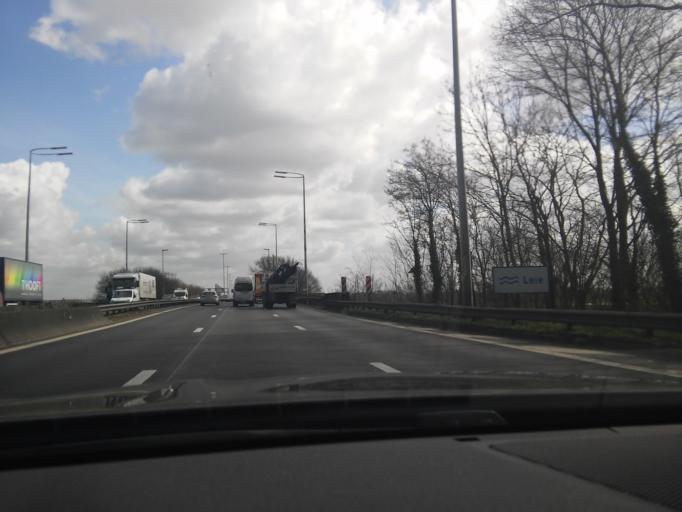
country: BE
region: Flanders
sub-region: Provincie Oost-Vlaanderen
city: Sint-Martens-Latem
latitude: 51.0326
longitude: 3.6440
